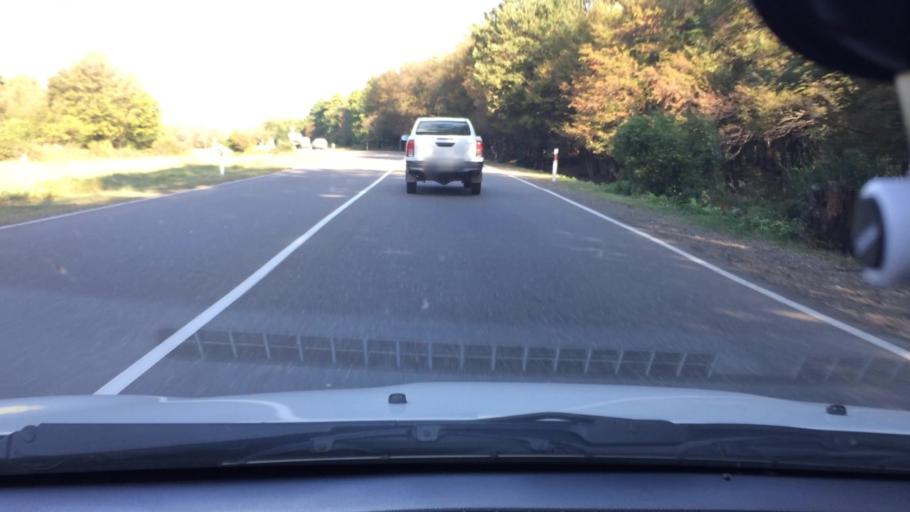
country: GE
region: Imereti
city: Kutaisi
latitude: 42.2292
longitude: 42.7792
